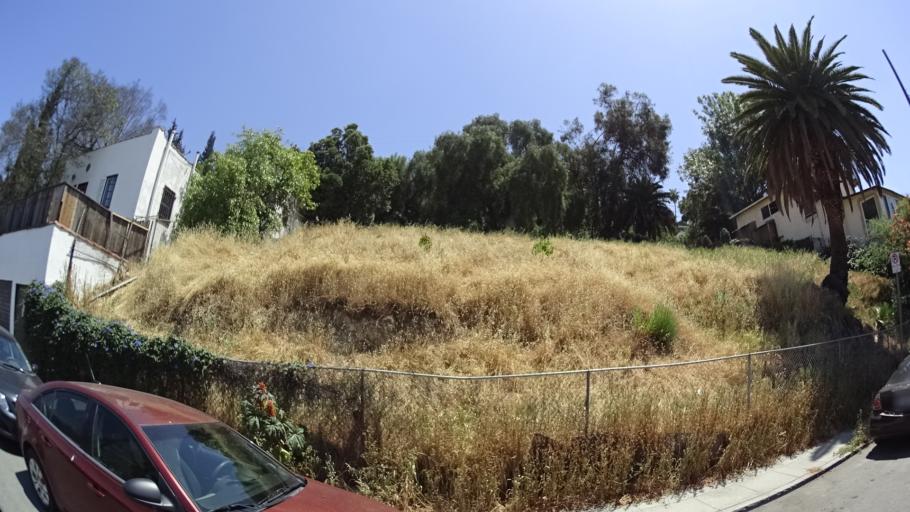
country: US
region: California
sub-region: Los Angeles County
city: Echo Park
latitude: 34.0789
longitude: -118.2552
